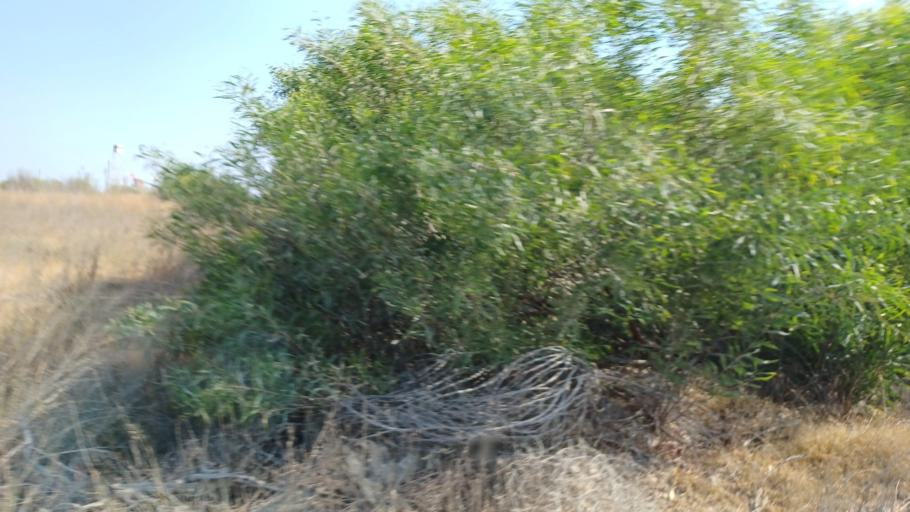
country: CY
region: Ammochostos
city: Deryneia
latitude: 35.0675
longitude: 33.9844
